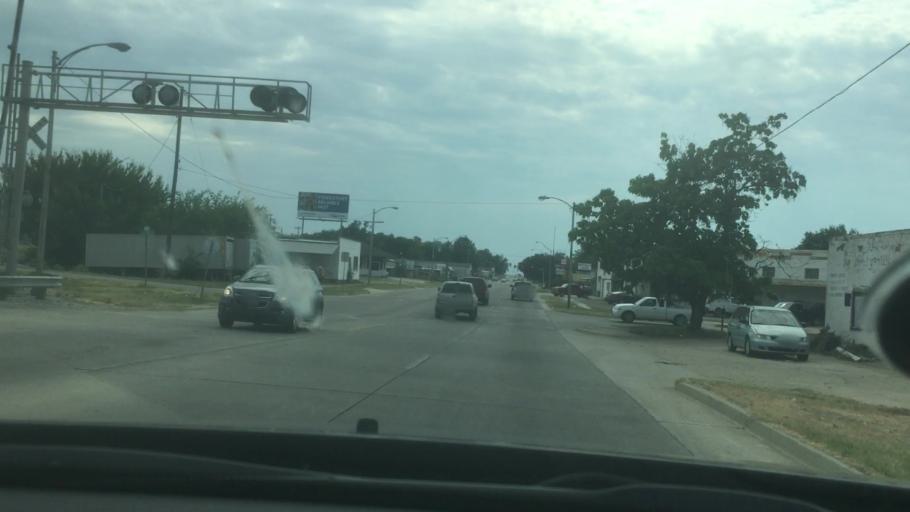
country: US
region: Oklahoma
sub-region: Pontotoc County
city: Ada
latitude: 34.7745
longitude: -96.6829
